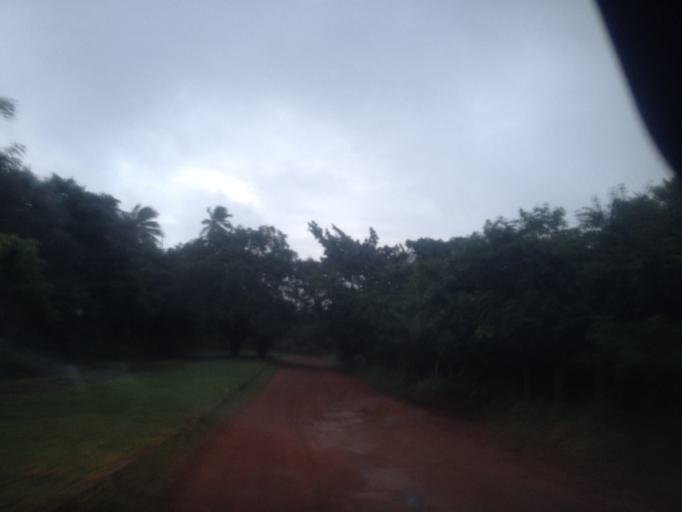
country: BR
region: Bahia
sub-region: Mata De Sao Joao
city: Mata de Sao Joao
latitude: -12.5778
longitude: -38.0302
